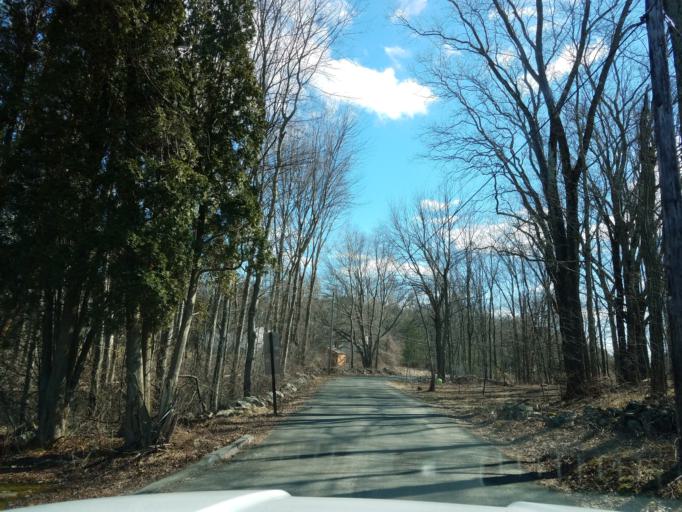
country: US
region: Connecticut
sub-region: Windham County
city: North Grosvenor Dale
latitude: 41.9965
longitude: -71.8848
